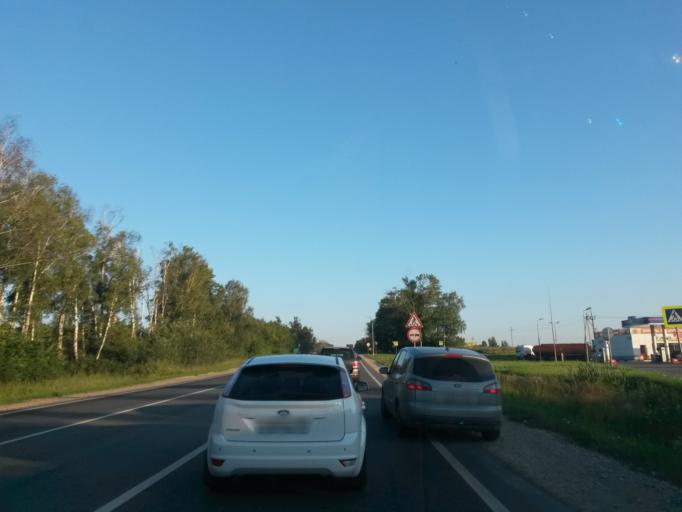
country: RU
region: Moskovskaya
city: Belyye Stolby
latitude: 55.3241
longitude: 37.8072
